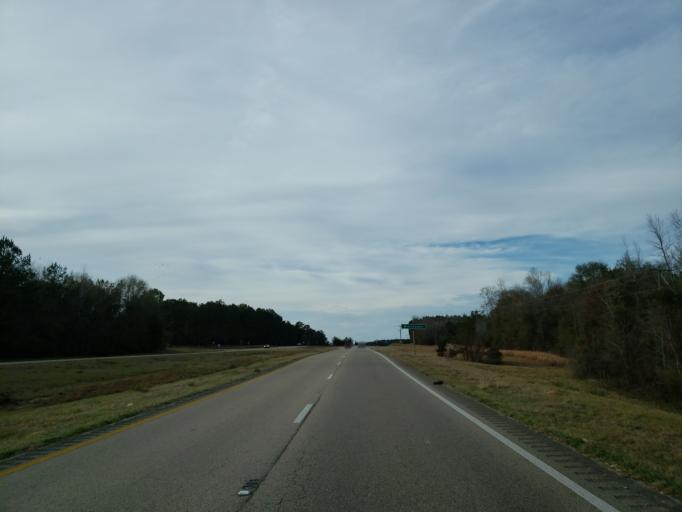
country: US
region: Mississippi
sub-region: Wayne County
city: Waynesboro
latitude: 31.6250
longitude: -88.5860
